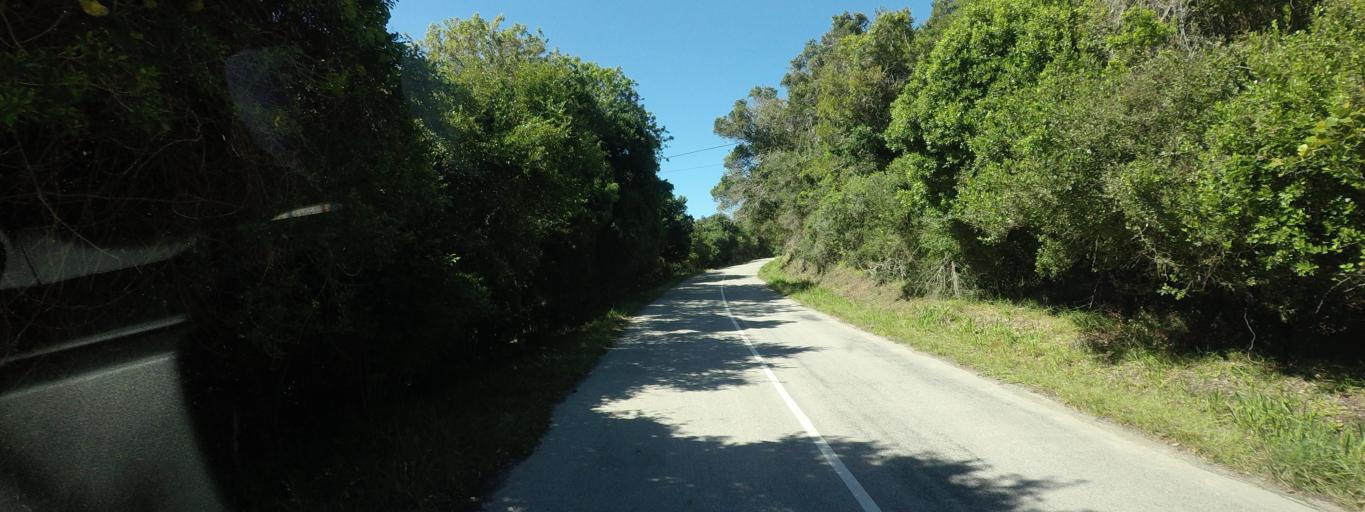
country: ZA
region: Western Cape
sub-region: Eden District Municipality
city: Plettenberg Bay
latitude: -33.9709
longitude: 23.5618
